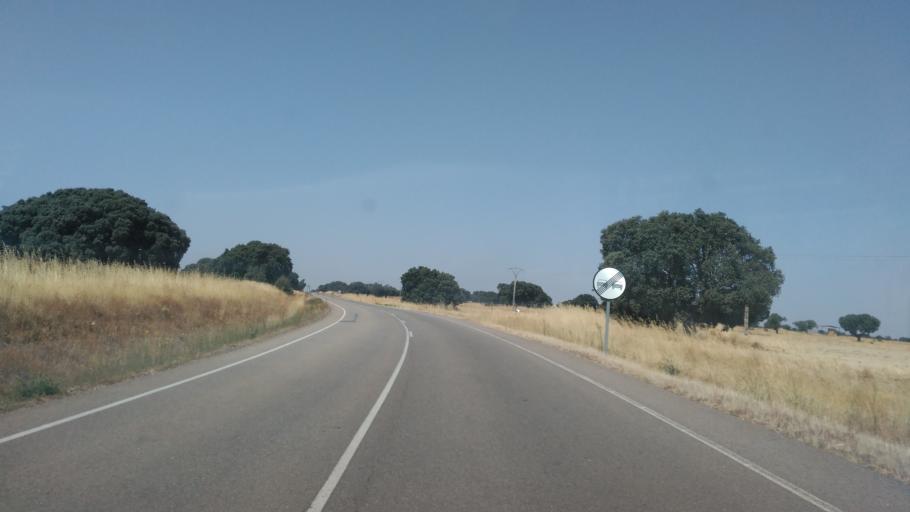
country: ES
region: Castille and Leon
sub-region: Provincia de Salamanca
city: Cabrillas
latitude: 40.7554
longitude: -6.1883
